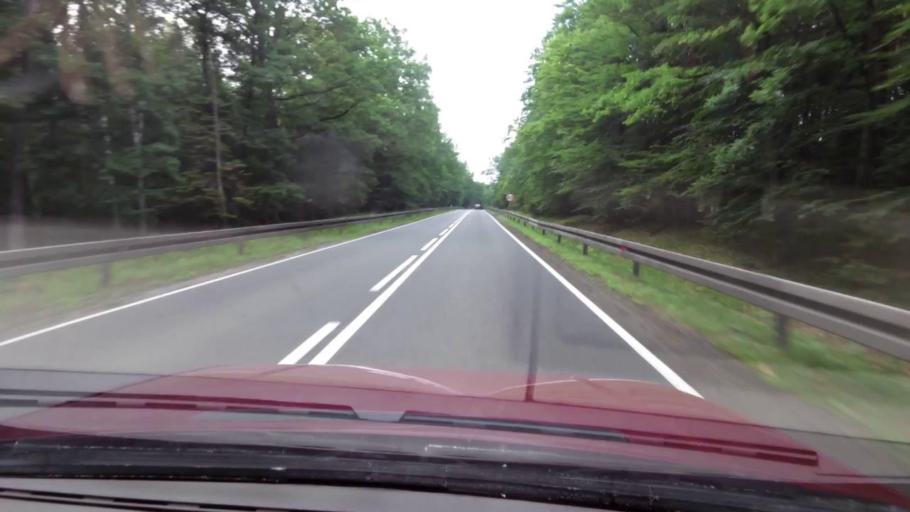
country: PL
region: Pomeranian Voivodeship
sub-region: Powiat bytowski
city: Trzebielino
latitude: 54.2279
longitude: 17.0868
